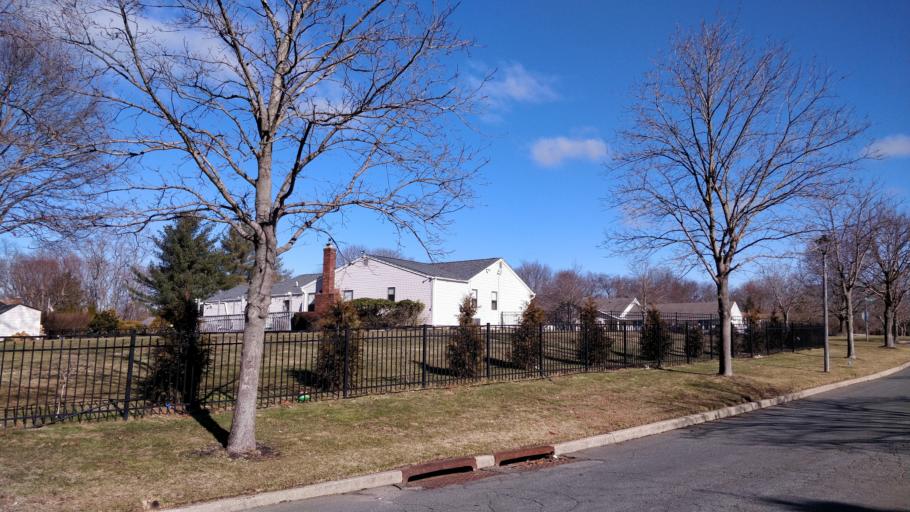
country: US
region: New York
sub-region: Suffolk County
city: Saint James
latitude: 40.8836
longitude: -73.1439
